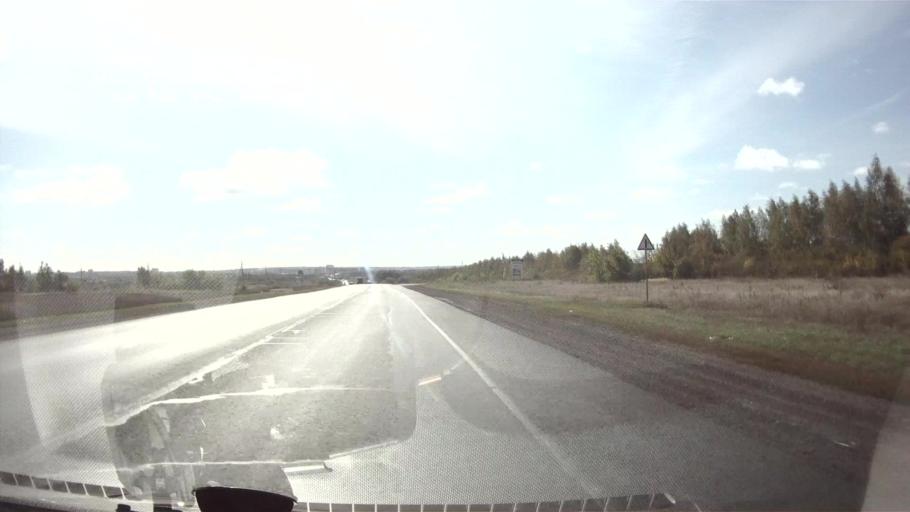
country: RU
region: Ulyanovsk
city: Isheyevka
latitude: 54.3130
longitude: 48.2347
